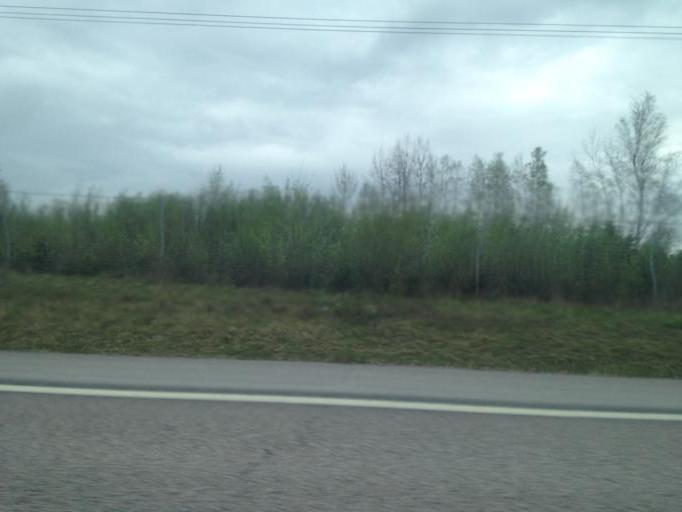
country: FI
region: Uusimaa
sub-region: Helsinki
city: Nurmijaervi
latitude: 60.4692
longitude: 24.8501
